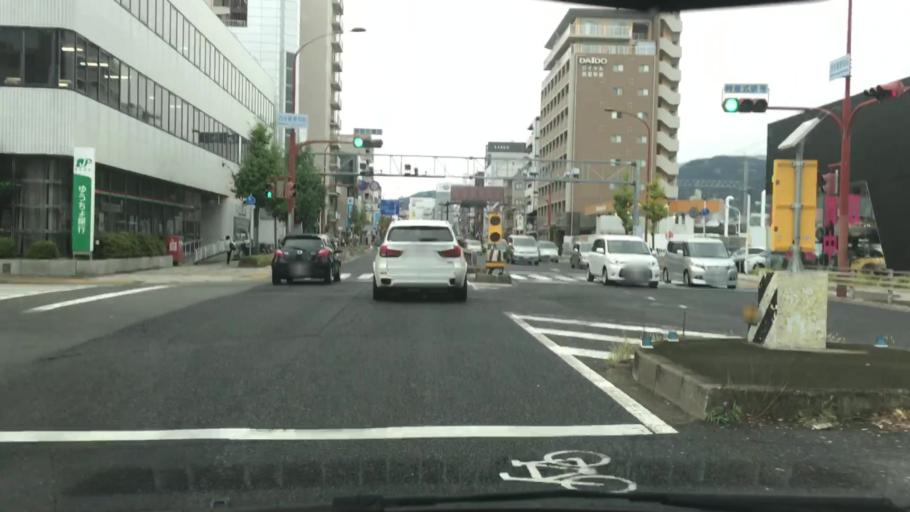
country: JP
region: Hyogo
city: Nishinomiya-hama
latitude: 34.7386
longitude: 135.3384
